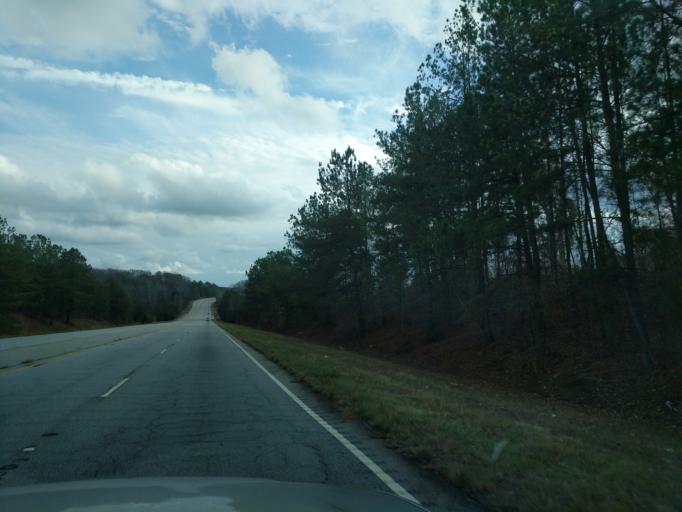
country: US
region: South Carolina
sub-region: Greenwood County
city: Ware Shoals
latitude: 34.4140
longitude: -82.2297
